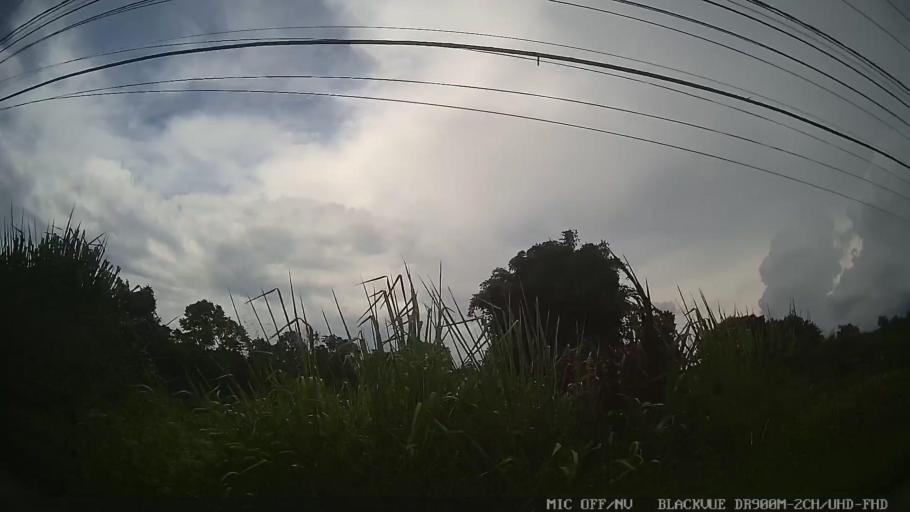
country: BR
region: Sao Paulo
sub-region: Suzano
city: Suzano
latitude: -23.4886
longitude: -46.2692
